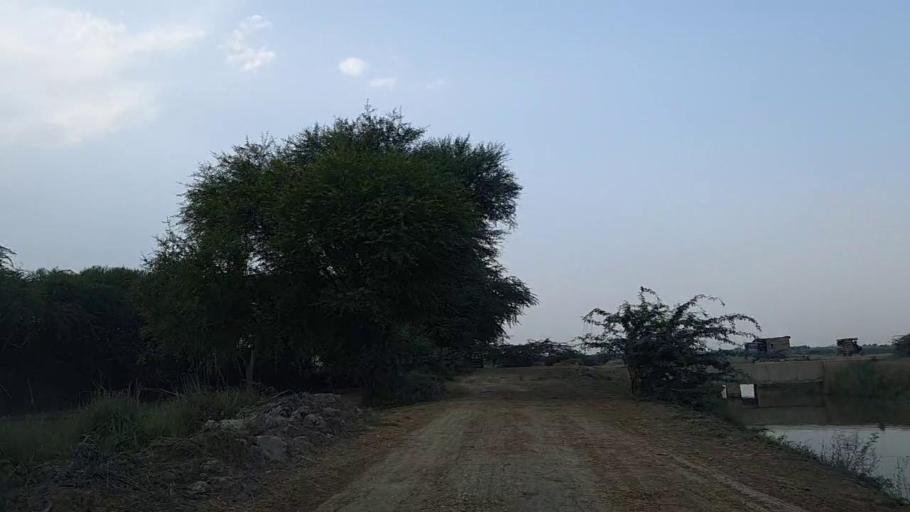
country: PK
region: Sindh
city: Daro Mehar
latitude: 24.7662
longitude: 68.1347
